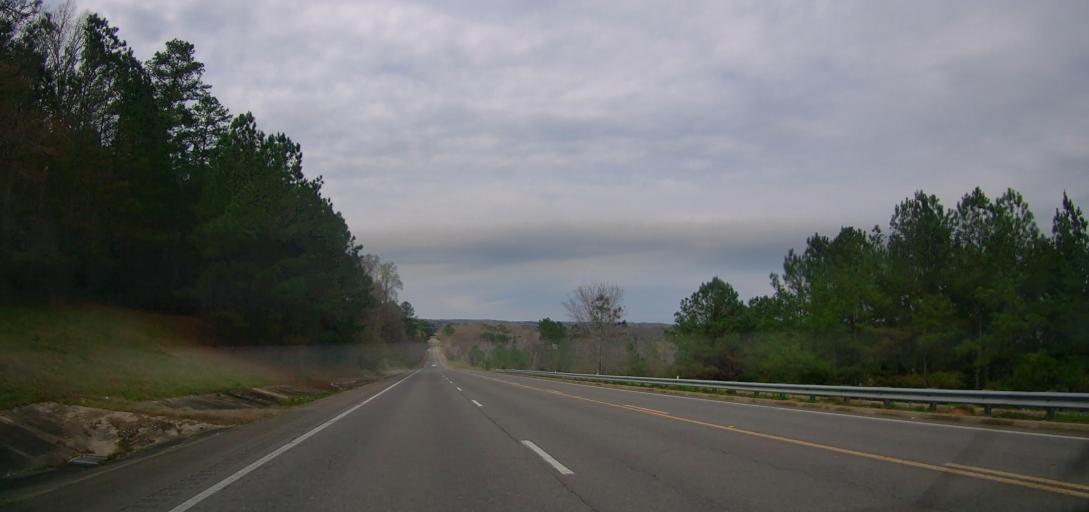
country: US
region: Alabama
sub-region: Marion County
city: Hamilton
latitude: 34.0868
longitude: -87.9804
